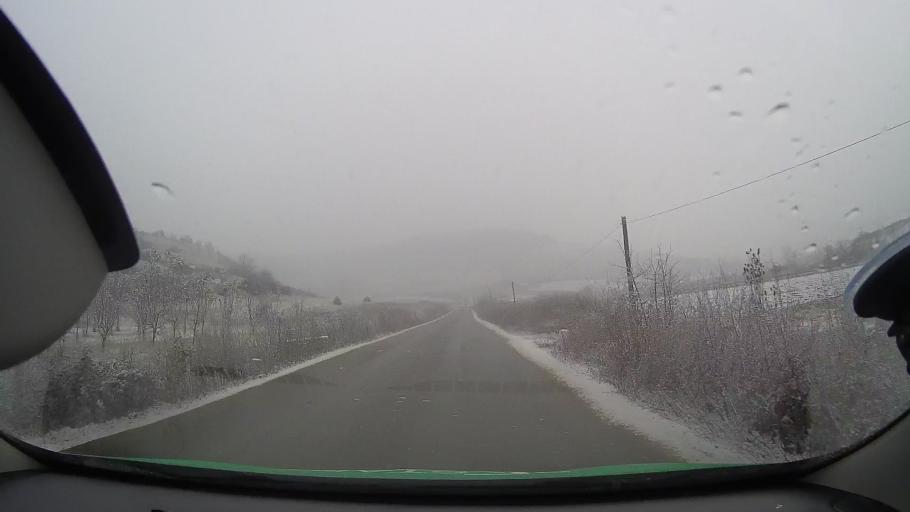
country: RO
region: Alba
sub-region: Municipiul Aiud
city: Ciumbrud
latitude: 46.3116
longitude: 23.7776
